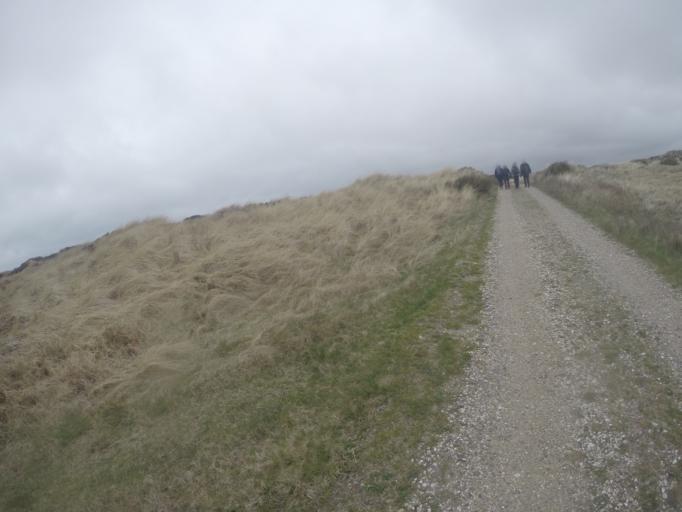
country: DK
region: North Denmark
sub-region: Thisted Kommune
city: Hurup
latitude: 56.8631
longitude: 8.2920
